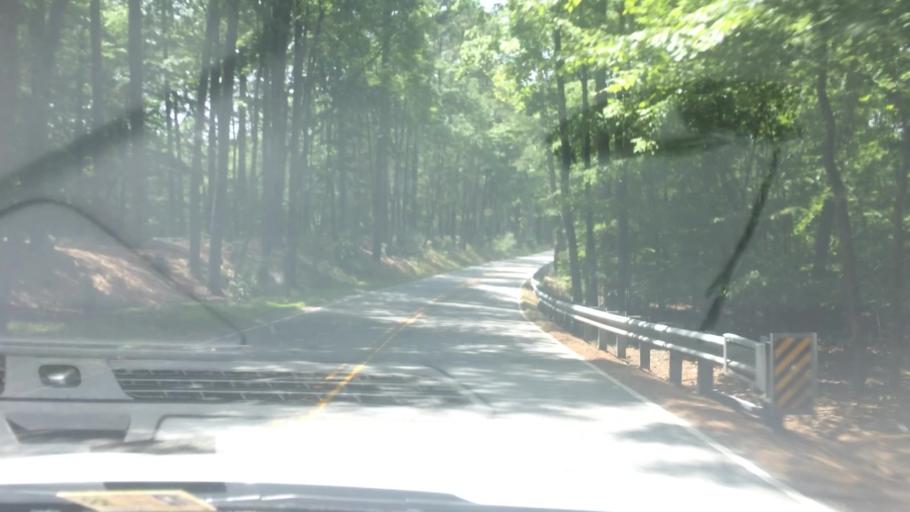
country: US
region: Virginia
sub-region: City of Williamsburg
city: Williamsburg
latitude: 37.3171
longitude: -76.7044
